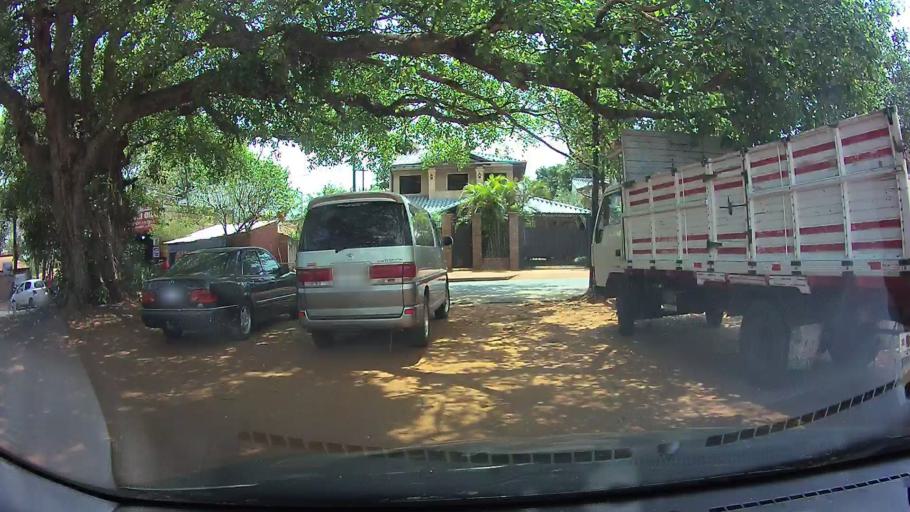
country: PY
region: Central
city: Itaugua
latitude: -25.3908
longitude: -57.3555
